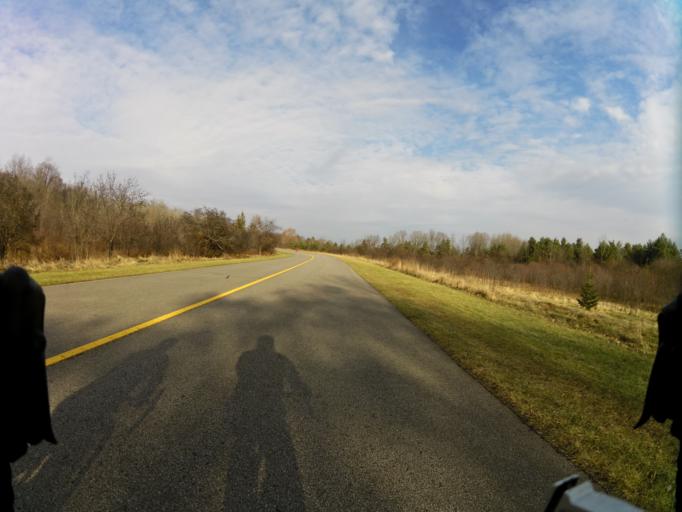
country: CA
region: Quebec
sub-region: Outaouais
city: Gatineau
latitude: 45.4430
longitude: -75.7603
